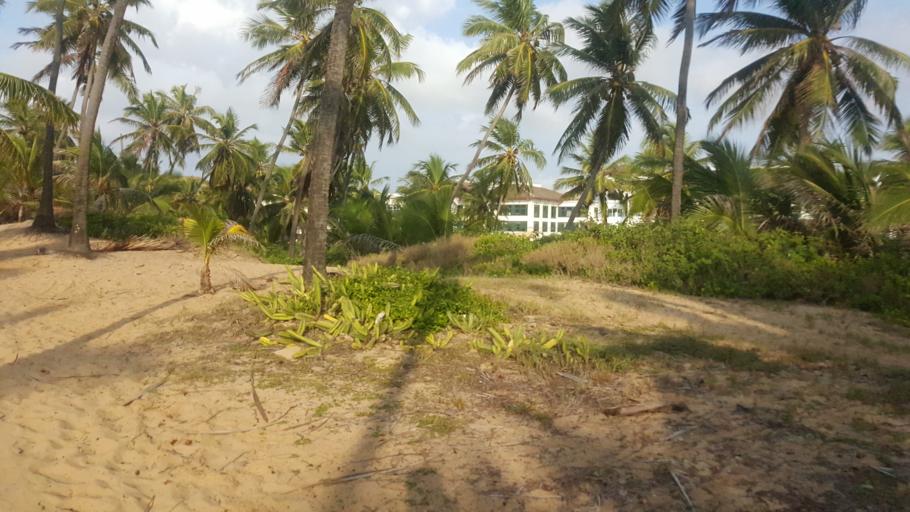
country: BR
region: Bahia
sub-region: Mata De Sao Joao
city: Mata de Sao Joao
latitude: -12.4427
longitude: -37.9214
